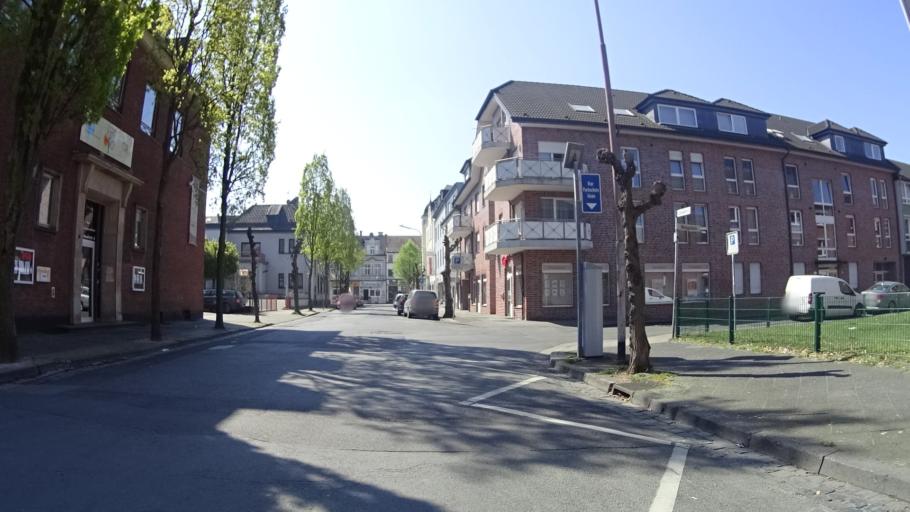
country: DE
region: North Rhine-Westphalia
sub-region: Regierungsbezirk Dusseldorf
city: Moers
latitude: 51.4515
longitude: 6.6327
